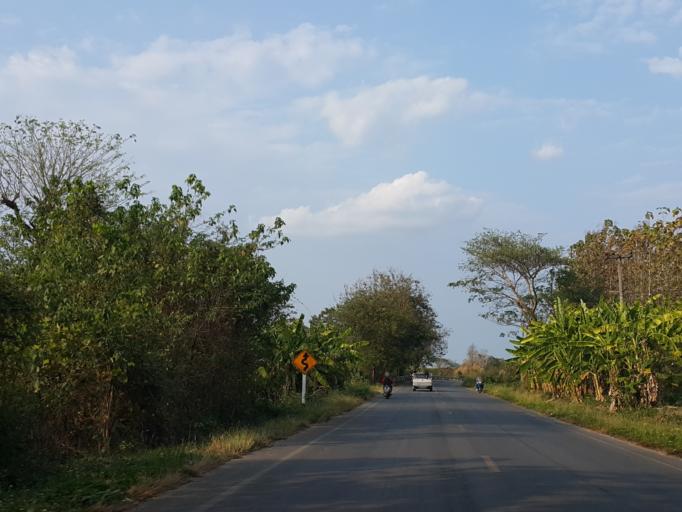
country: TH
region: Lampang
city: Hang Chat
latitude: 18.4459
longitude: 99.4516
